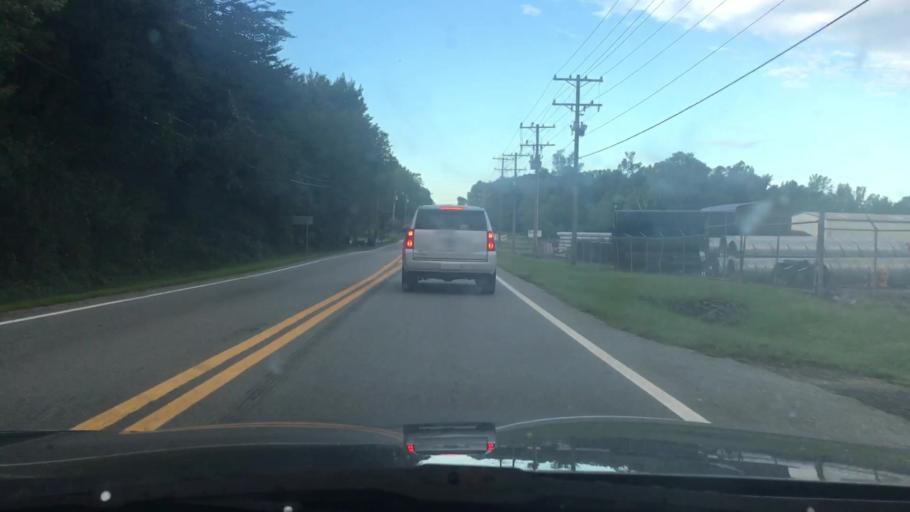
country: US
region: North Carolina
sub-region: Alamance County
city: Green Level
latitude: 36.1283
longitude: -79.3464
